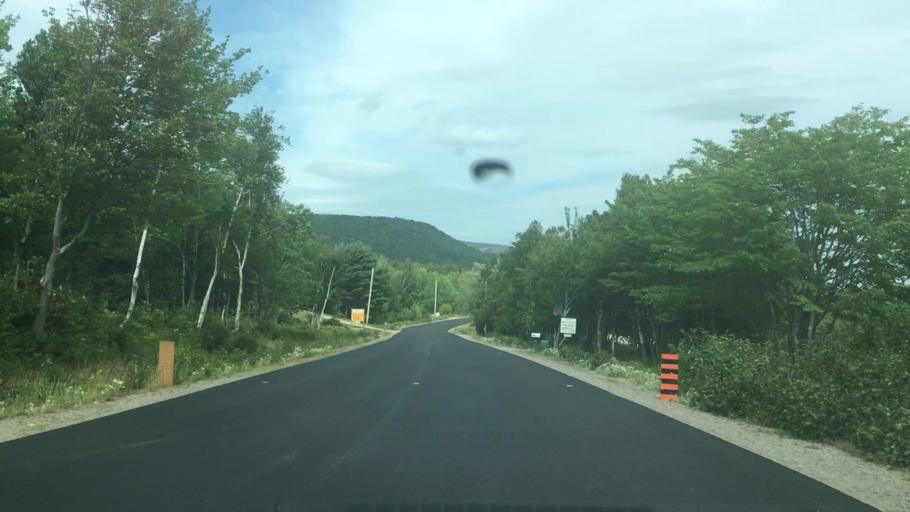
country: CA
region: Nova Scotia
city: Sydney Mines
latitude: 46.5483
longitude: -60.4122
